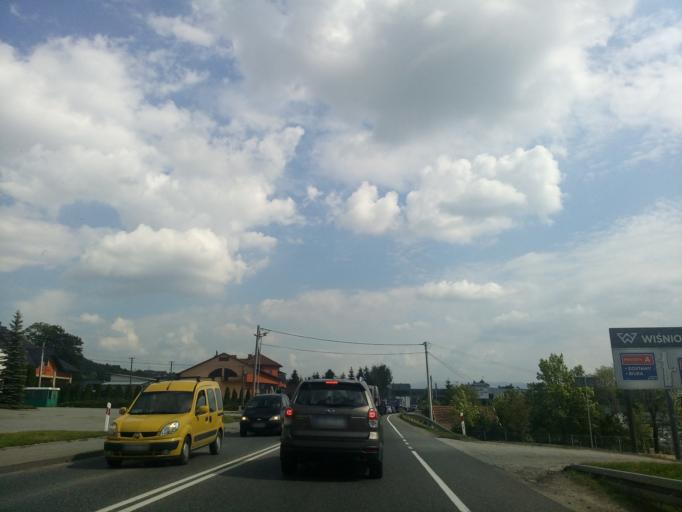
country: PL
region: Lesser Poland Voivodeship
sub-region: Powiat nowosadecki
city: Chelmiec
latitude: 49.6720
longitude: 20.6852
